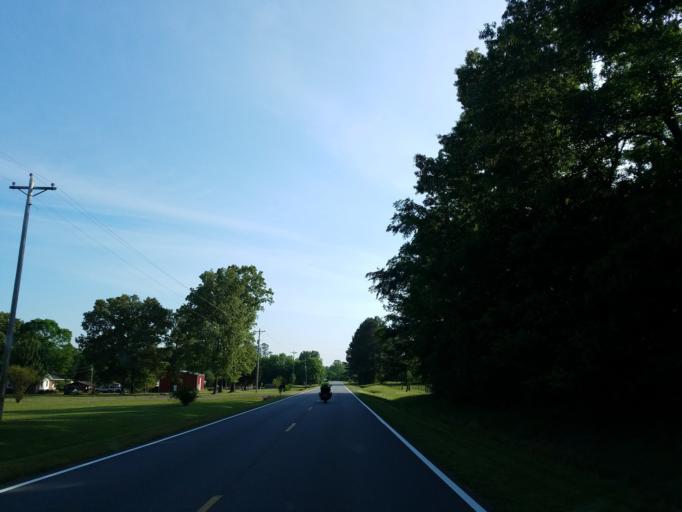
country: US
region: Georgia
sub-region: Chattooga County
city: Trion
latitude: 34.5452
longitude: -85.2019
